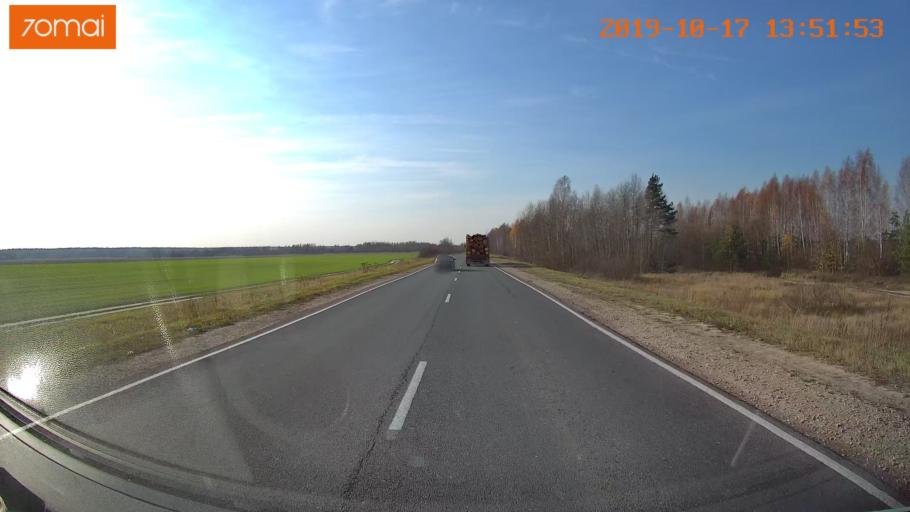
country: RU
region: Rjazan
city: Tuma
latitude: 55.1396
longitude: 40.3775
